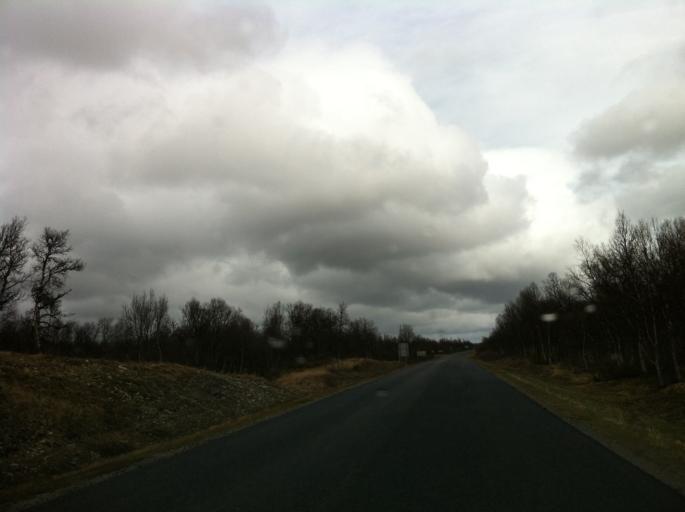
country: NO
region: Sor-Trondelag
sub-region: Tydal
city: Aas
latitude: 62.6410
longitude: 12.0644
